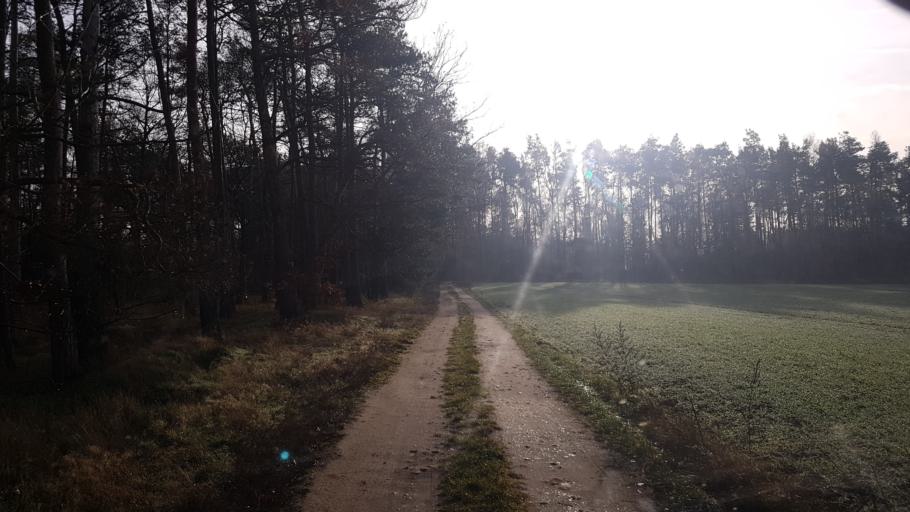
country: DE
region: Brandenburg
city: Ruckersdorf
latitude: 51.5923
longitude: 13.5559
